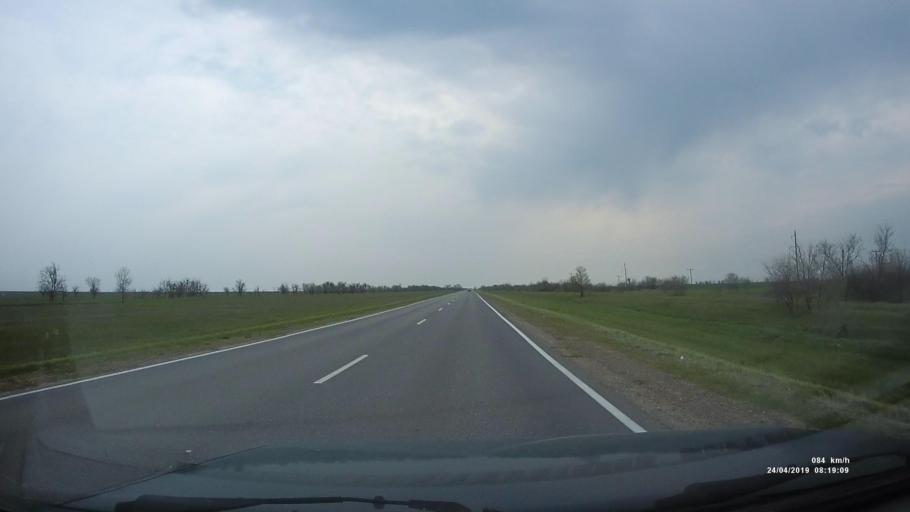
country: RU
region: Kalmykiya
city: Priyutnoye
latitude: 46.1031
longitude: 43.6602
